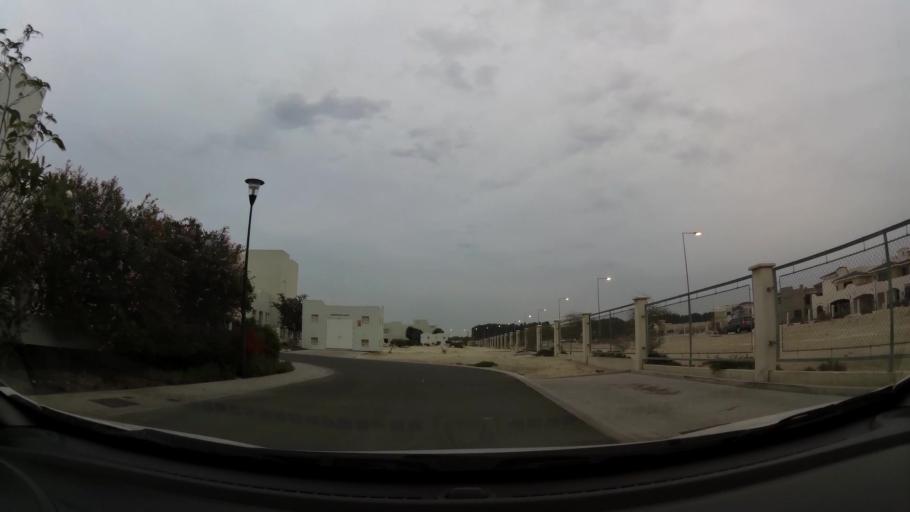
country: BH
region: Northern
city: Ar Rifa'
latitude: 26.0943
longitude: 50.5598
